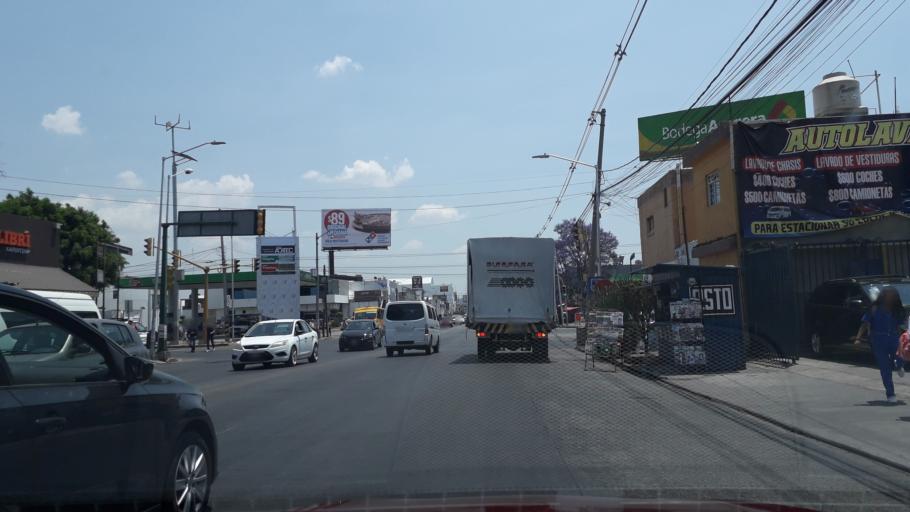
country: MX
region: Puebla
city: Puebla
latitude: 19.0367
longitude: -98.2135
